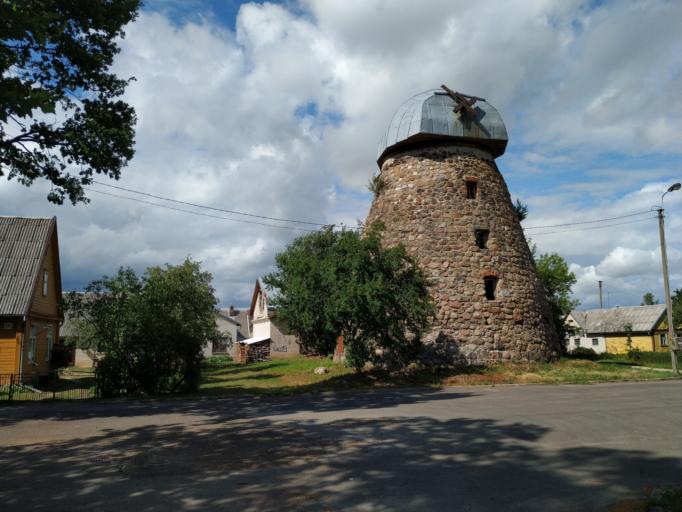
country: LT
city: Kupiskis
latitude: 55.8412
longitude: 24.9831
